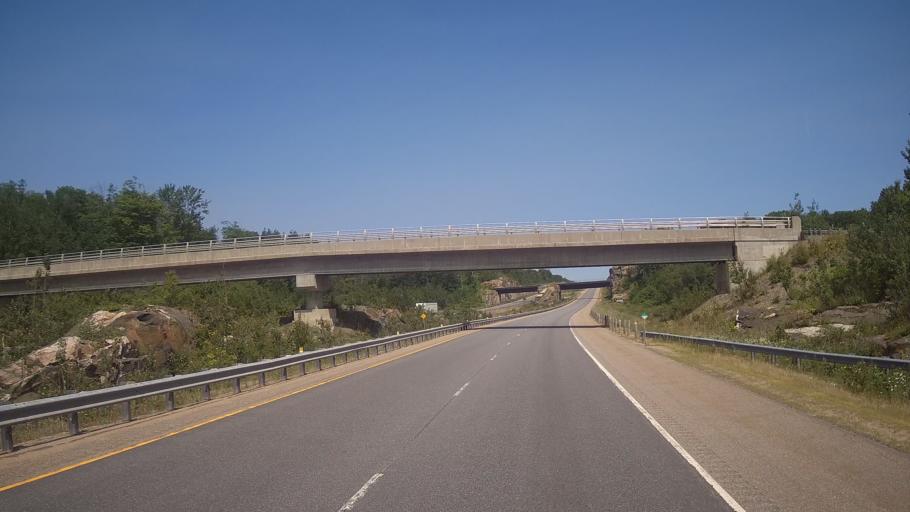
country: CA
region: Ontario
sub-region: Parry Sound District
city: Parry Sound
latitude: 45.2071
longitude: -79.8165
